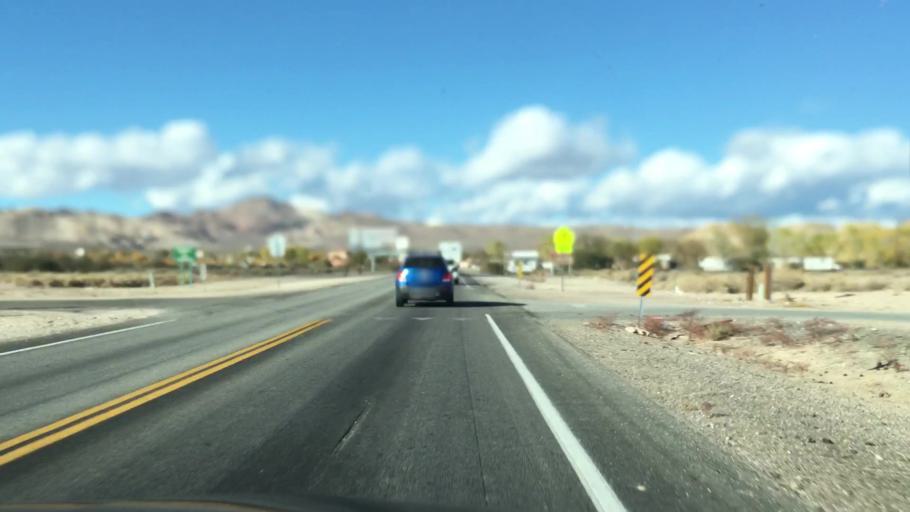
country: US
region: Nevada
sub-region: Nye County
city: Beatty
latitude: 36.9002
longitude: -116.7540
